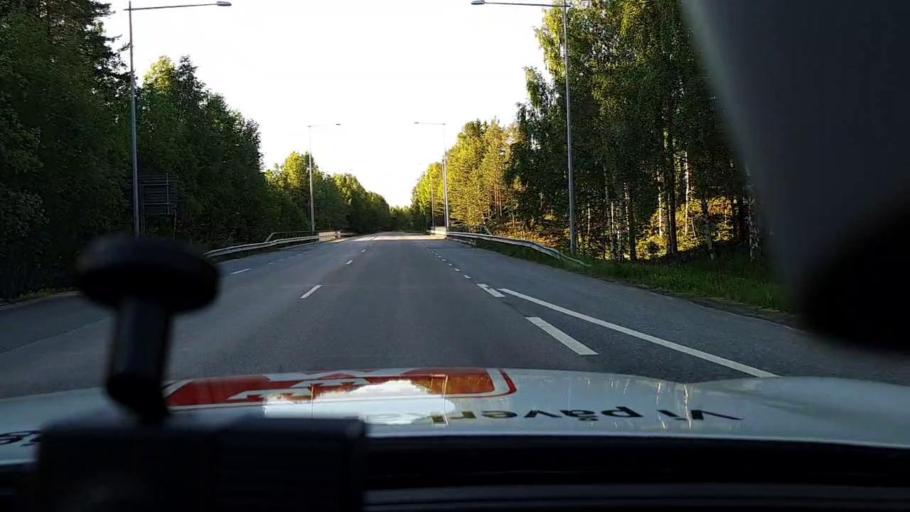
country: SE
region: Norrbotten
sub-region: Lulea Kommun
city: Lulea
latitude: 65.6078
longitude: 22.1867
